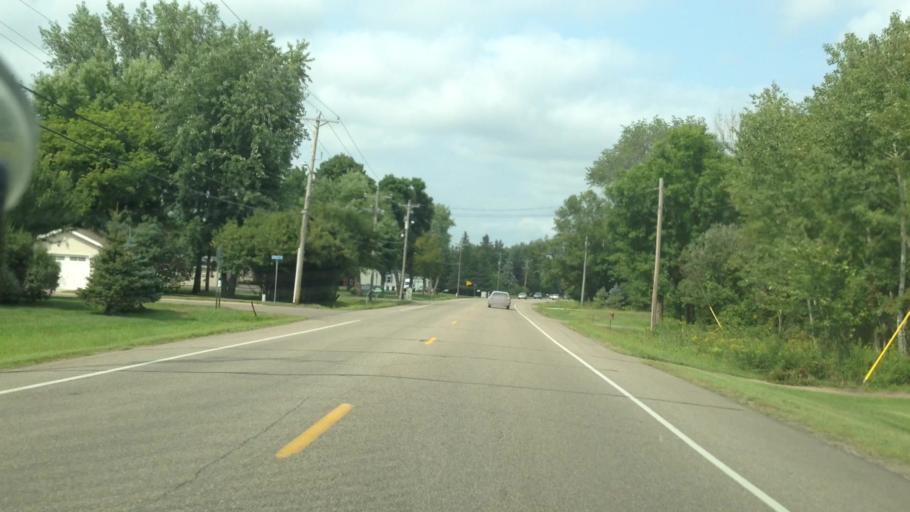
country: US
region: Minnesota
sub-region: Anoka County
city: Circle Pines
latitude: 45.1348
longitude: -93.1273
